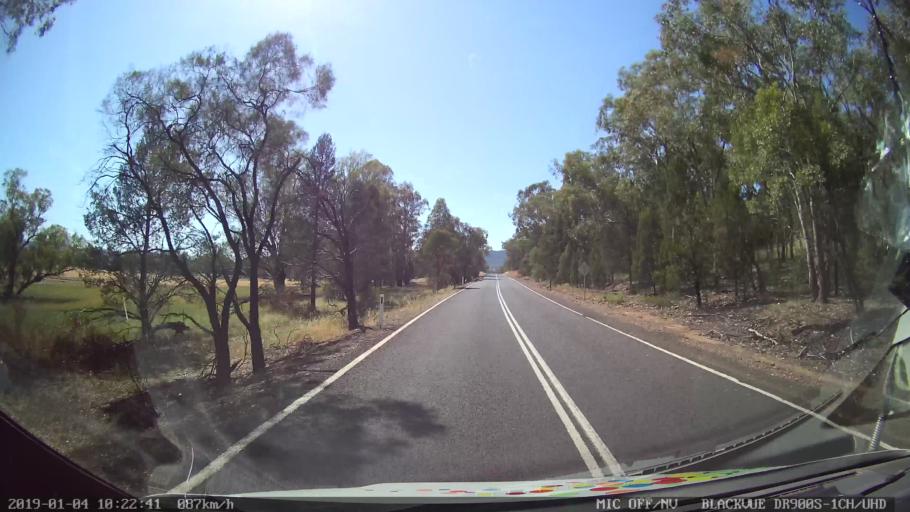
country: AU
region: New South Wales
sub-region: Cabonne
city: Canowindra
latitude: -33.3684
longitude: 148.5291
